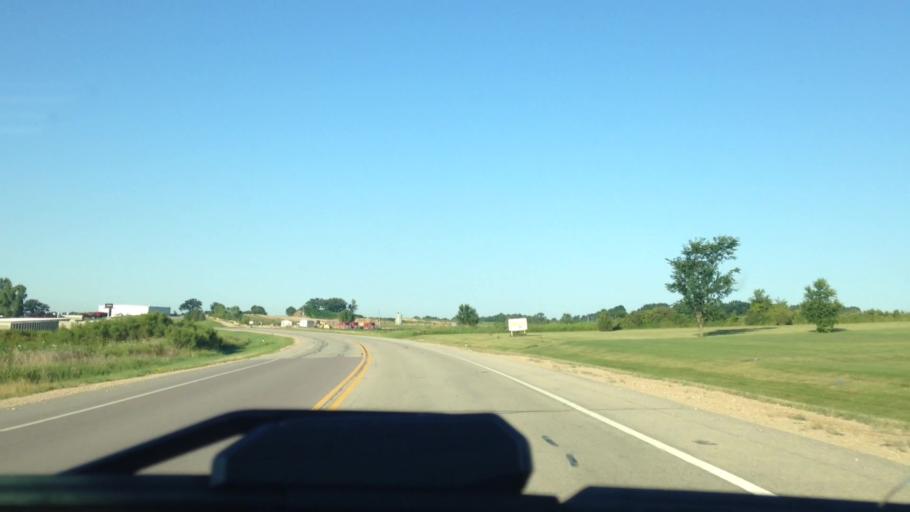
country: US
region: Wisconsin
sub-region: Columbia County
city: Columbus
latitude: 43.3483
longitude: -89.0422
